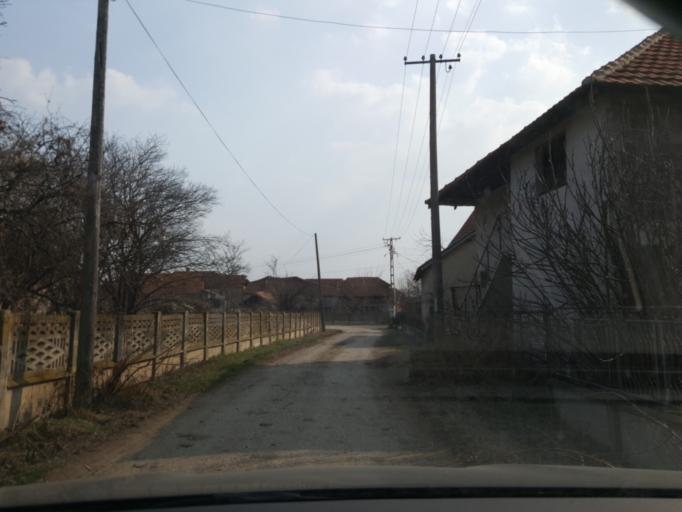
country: RS
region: Central Serbia
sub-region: Nisavski Okrug
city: Aleksinac
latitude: 43.4526
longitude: 21.7893
